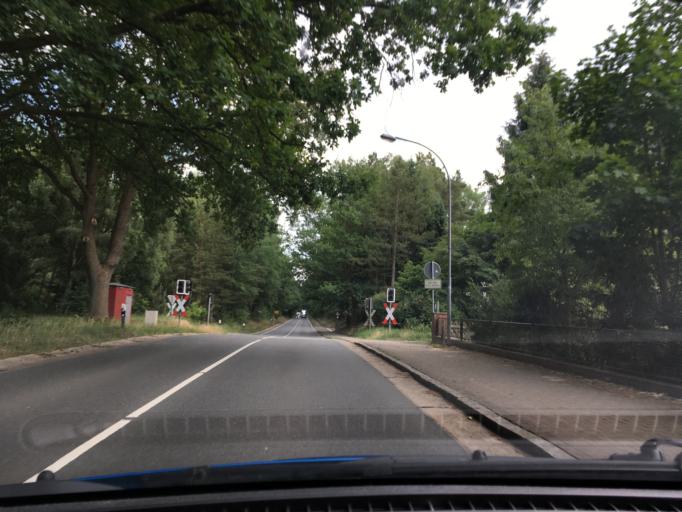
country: DE
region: Lower Saxony
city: Soderstorf
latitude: 53.1390
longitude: 10.1503
